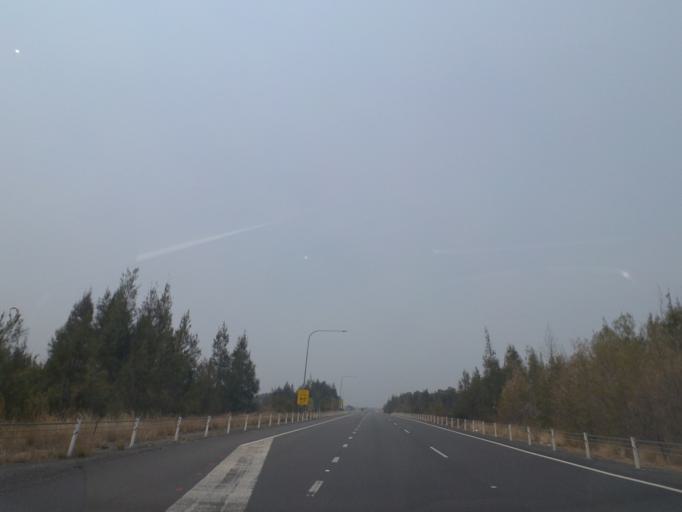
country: AU
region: New South Wales
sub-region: Ballina
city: Ballina
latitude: -28.8640
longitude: 153.5103
